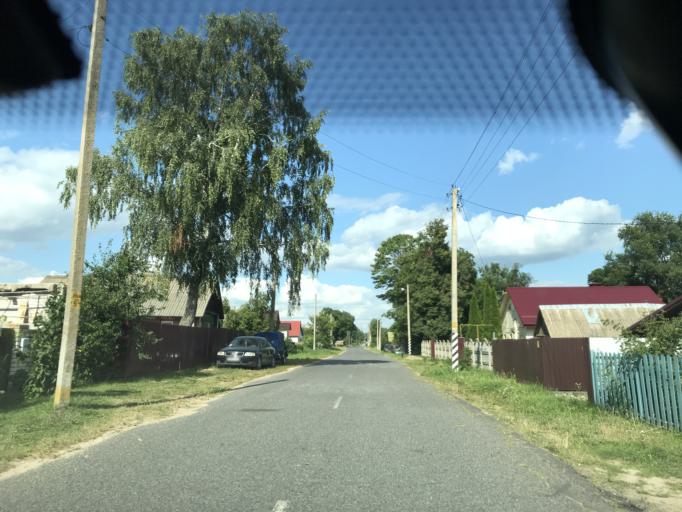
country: BY
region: Mogilev
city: Poselok Voskhod
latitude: 53.7855
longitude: 30.3537
